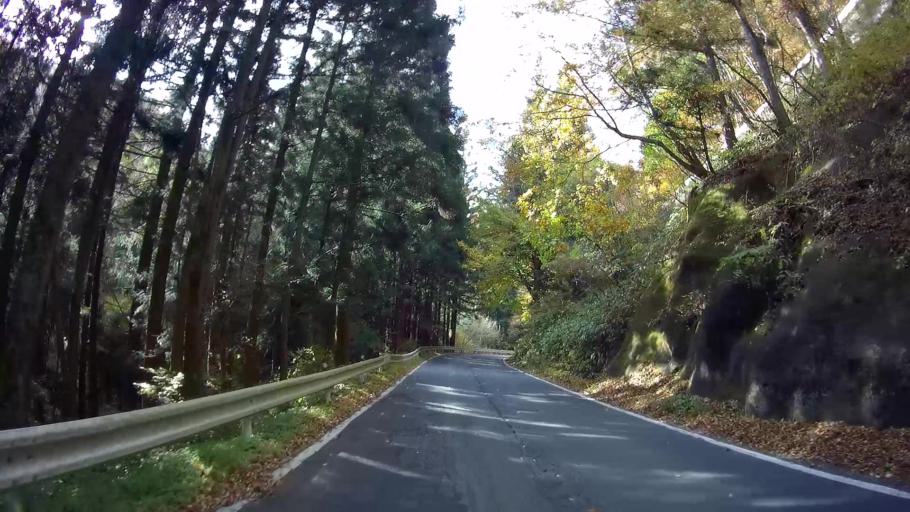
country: JP
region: Gunma
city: Nakanojomachi
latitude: 36.6168
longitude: 138.6364
